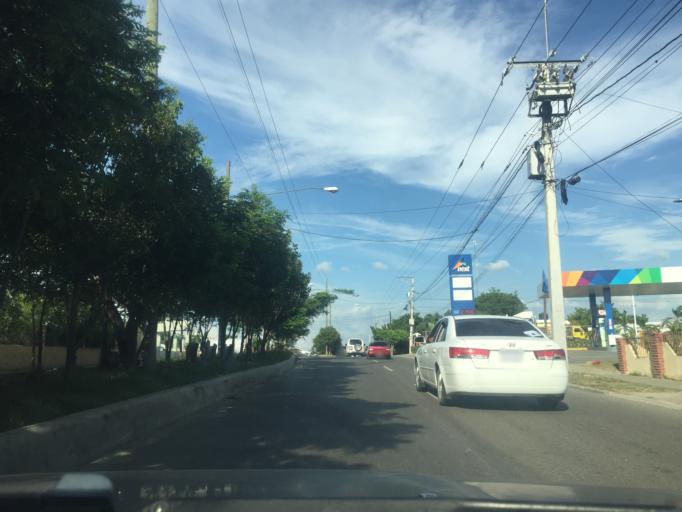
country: DO
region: Santiago
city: Santiago de los Caballeros
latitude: 19.4409
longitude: -70.7315
